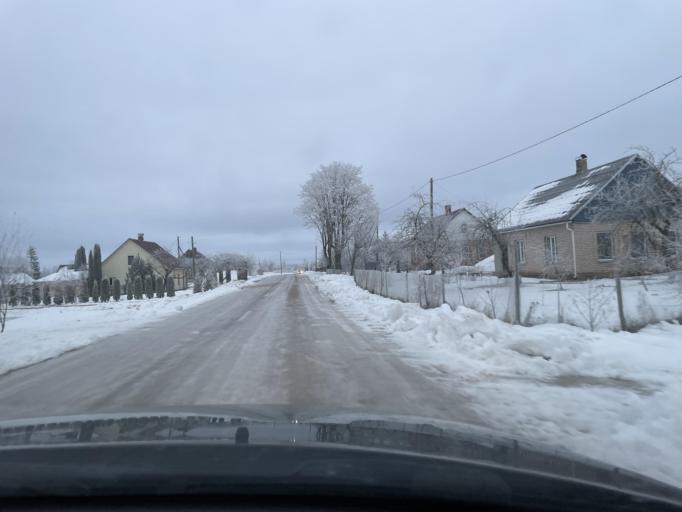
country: LV
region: Ludzas Rajons
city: Ludza
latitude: 56.4644
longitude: 27.5792
